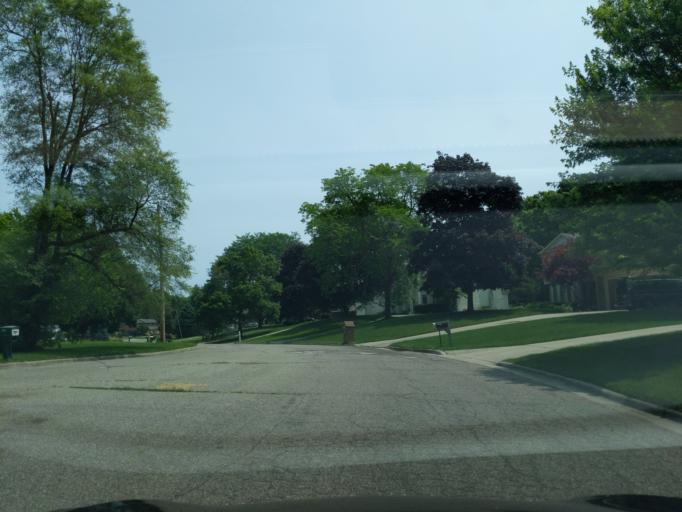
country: US
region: Michigan
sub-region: Eaton County
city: Waverly
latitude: 42.7600
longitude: -84.6470
